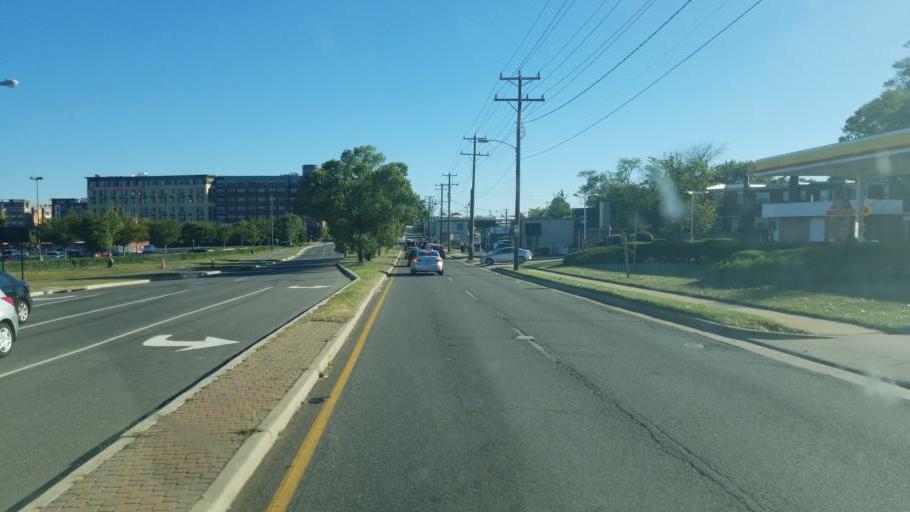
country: US
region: Virginia
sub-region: City of Alexandria
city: Alexandria
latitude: 38.8346
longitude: -77.0516
